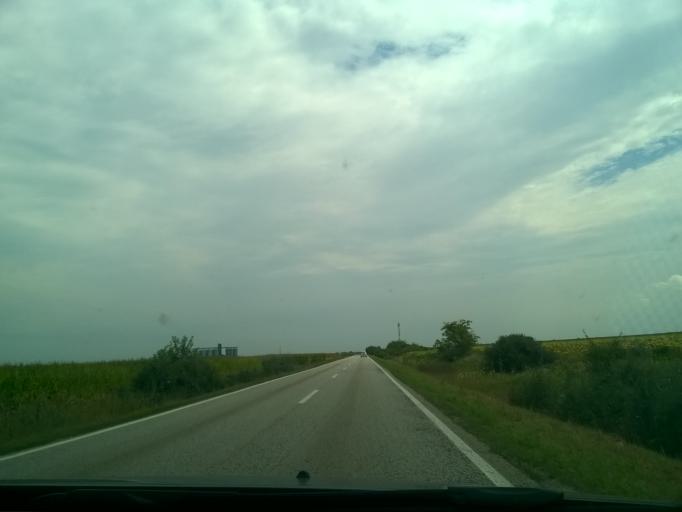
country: RS
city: Banatski Despotovac
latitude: 45.3799
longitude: 20.6643
